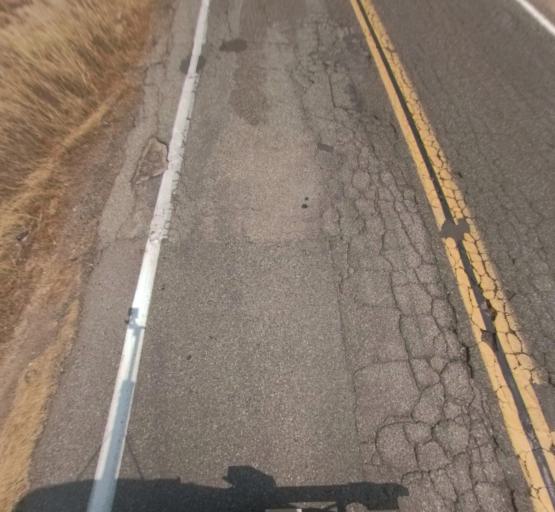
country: US
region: California
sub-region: Madera County
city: Yosemite Lakes
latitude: 37.1647
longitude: -119.9112
